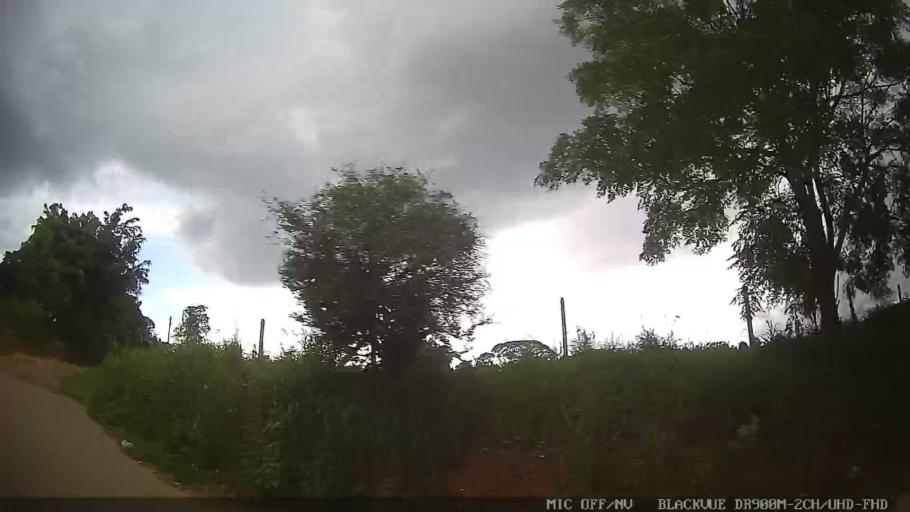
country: BR
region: Sao Paulo
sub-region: Suzano
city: Suzano
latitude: -23.6200
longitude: -46.2883
